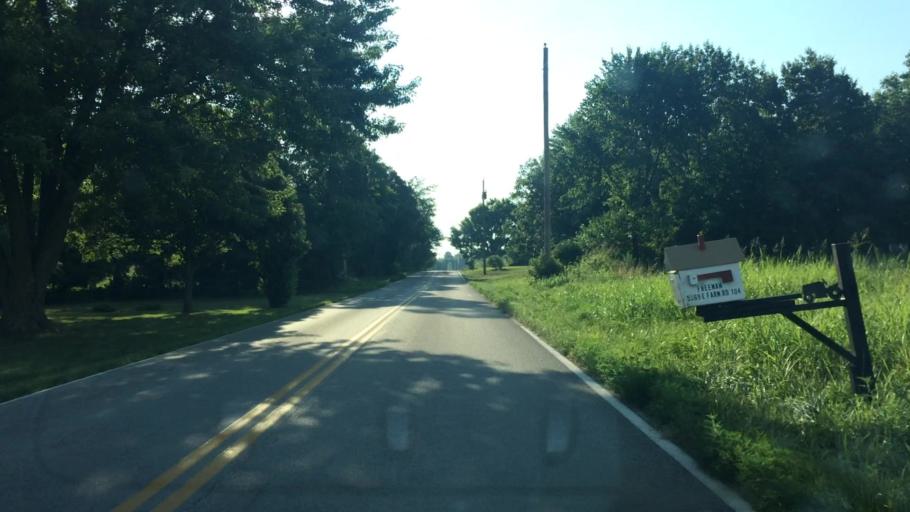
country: US
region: Missouri
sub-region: Greene County
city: Strafford
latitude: 37.2555
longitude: -93.1746
